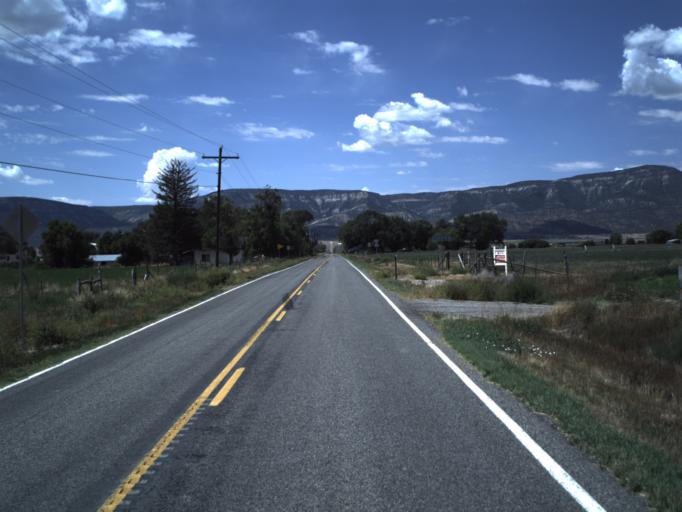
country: US
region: Utah
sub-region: Sanpete County
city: Moroni
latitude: 39.4762
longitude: -111.5576
